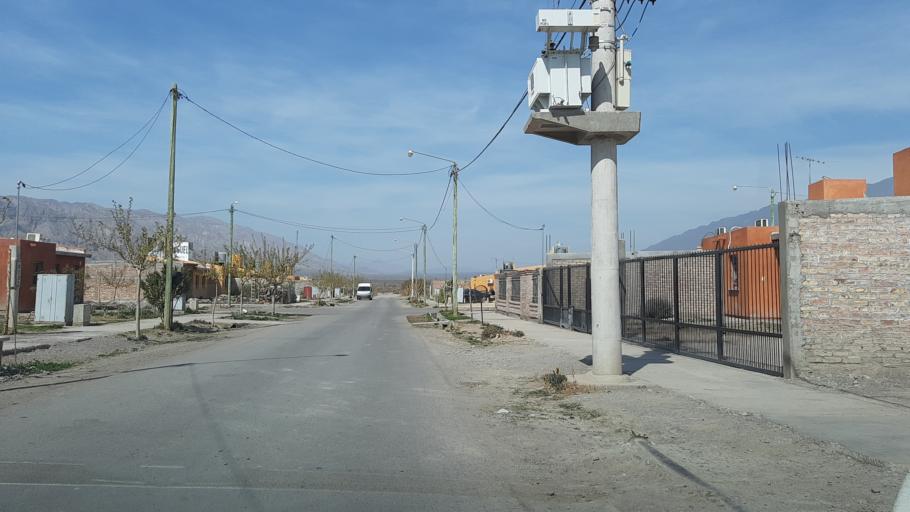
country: AR
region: San Juan
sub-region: Departamento de Zonda
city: Zonda
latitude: -31.5455
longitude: -68.7397
